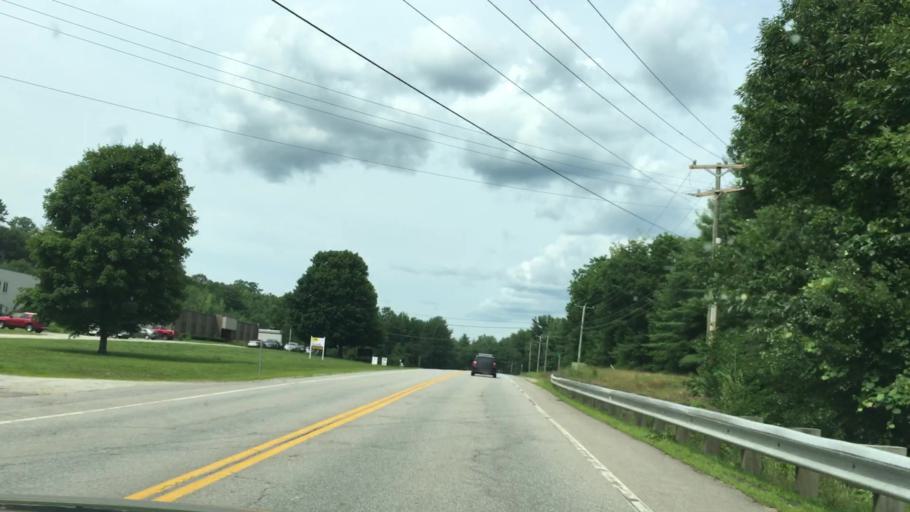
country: US
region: New Hampshire
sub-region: Hillsborough County
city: Peterborough
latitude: 42.8424
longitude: -71.9670
